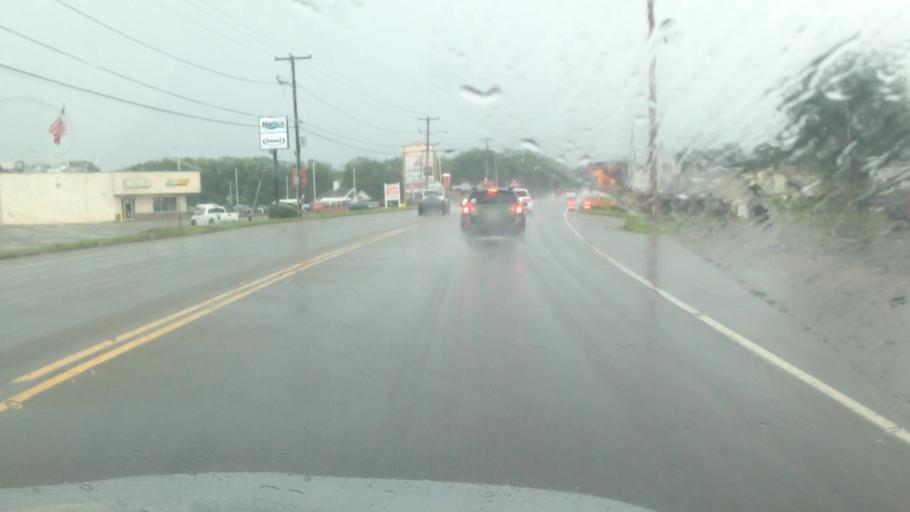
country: US
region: Massachusetts
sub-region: Worcester County
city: Auburn
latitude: 42.2112
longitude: -71.8017
